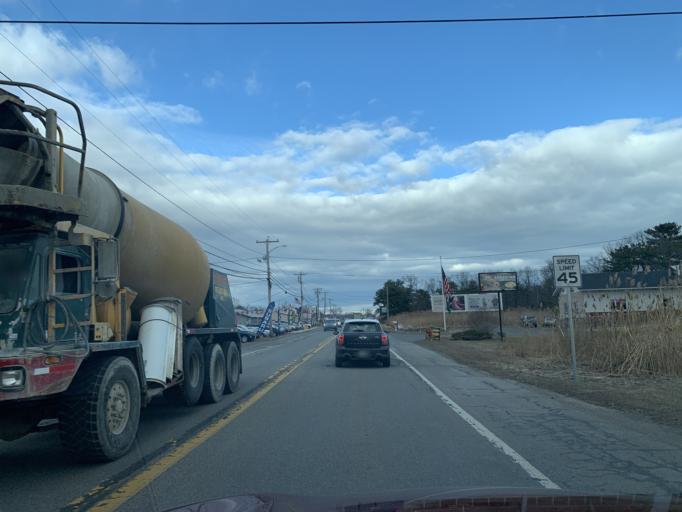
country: US
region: Massachusetts
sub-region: Essex County
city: Newburyport
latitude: 42.8222
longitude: -70.8670
